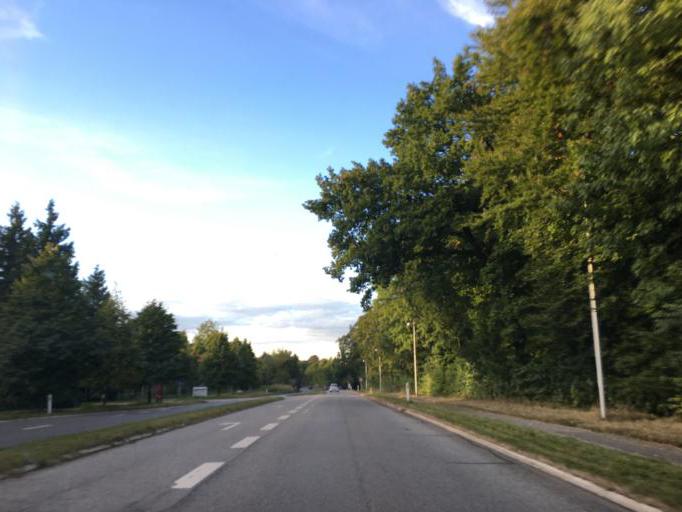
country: DK
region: Capital Region
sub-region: Horsholm Kommune
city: Horsholm
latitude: 55.8730
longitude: 12.4976
